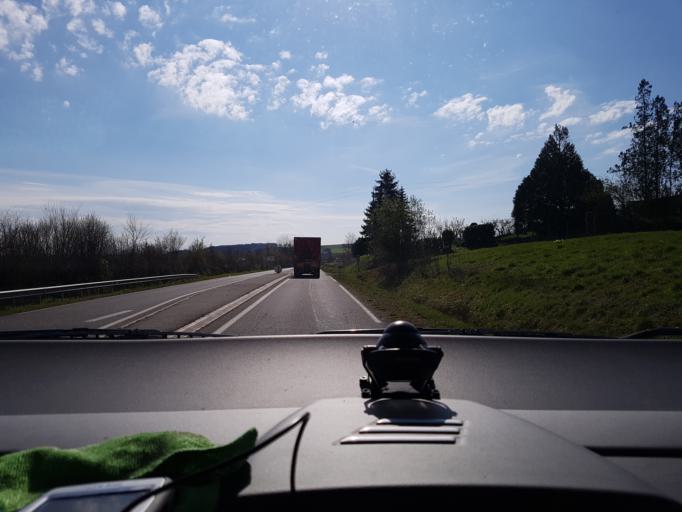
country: FR
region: Midi-Pyrenees
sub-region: Departement de l'Aveyron
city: Moyrazes
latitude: 44.3802
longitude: 2.4528
